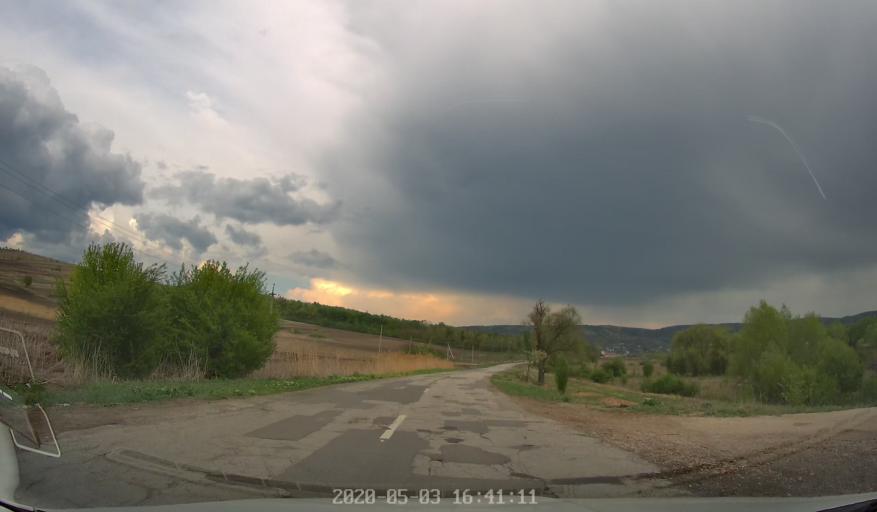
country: MD
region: Stinga Nistrului
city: Bucovat
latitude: 47.1691
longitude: 28.4044
